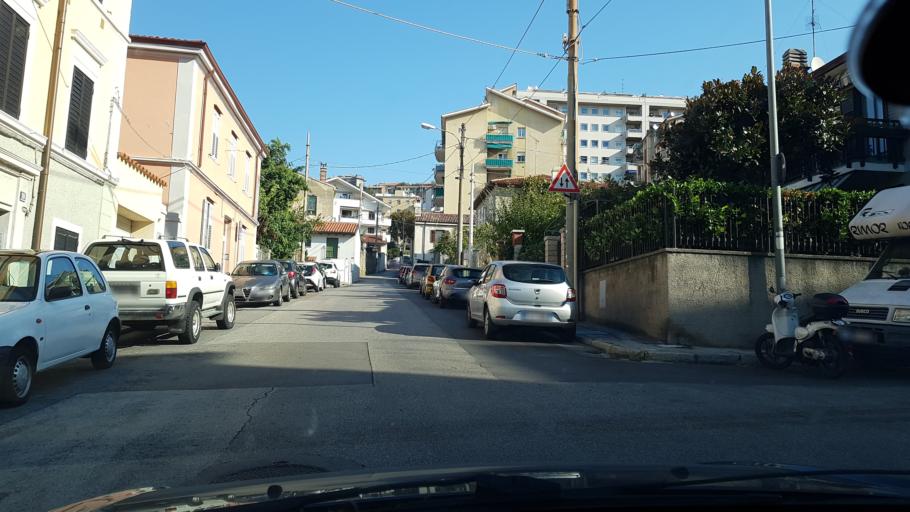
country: IT
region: Friuli Venezia Giulia
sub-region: Provincia di Trieste
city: Trieste
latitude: 45.6405
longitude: 13.7979
